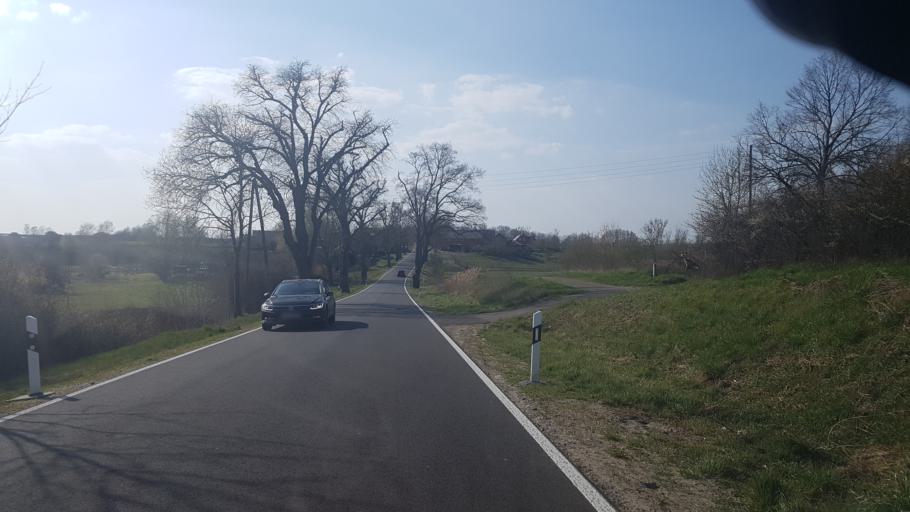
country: DE
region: Brandenburg
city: Gerswalde
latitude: 53.1605
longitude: 13.8230
